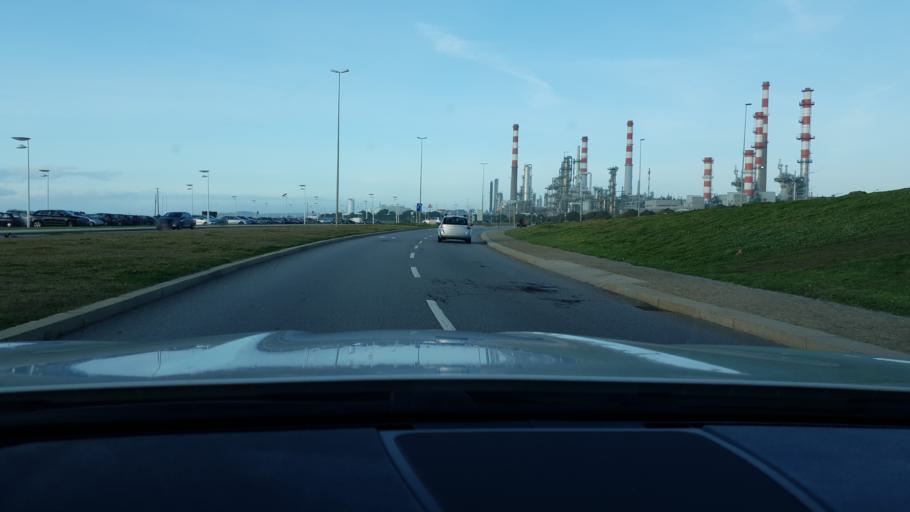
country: PT
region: Porto
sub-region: Matosinhos
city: Leca da Palmeira
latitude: 41.2072
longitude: -8.7147
